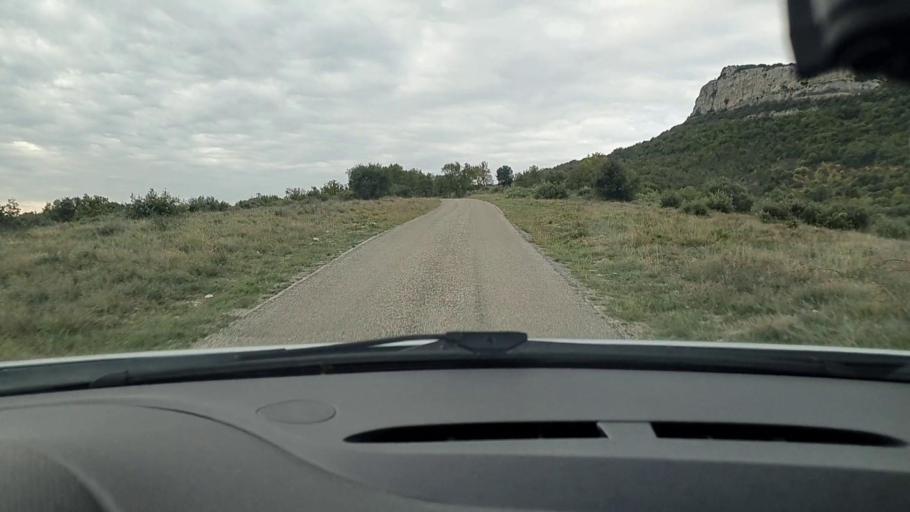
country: FR
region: Languedoc-Roussillon
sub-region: Departement du Gard
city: Mons
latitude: 44.1487
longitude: 4.2911
